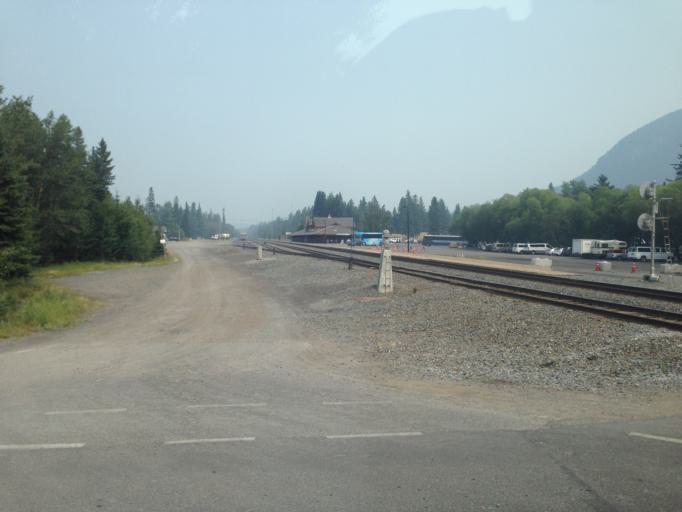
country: CA
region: Alberta
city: Banff
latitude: 51.1811
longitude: -115.5789
